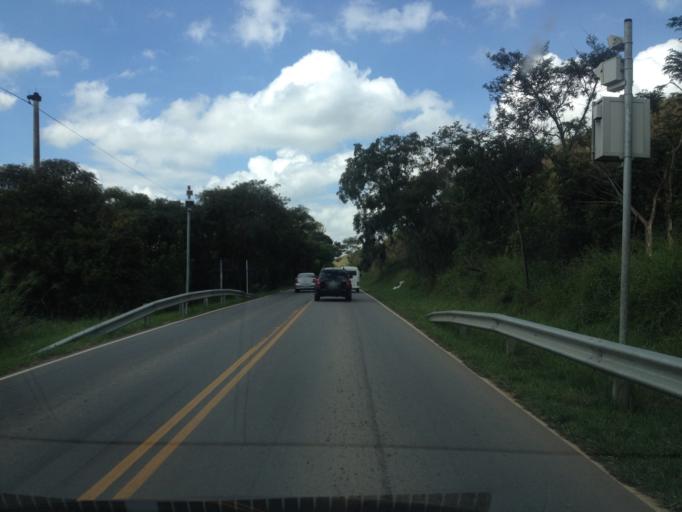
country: BR
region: Minas Gerais
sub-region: Itanhandu
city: Itanhandu
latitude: -22.2014
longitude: -44.9668
